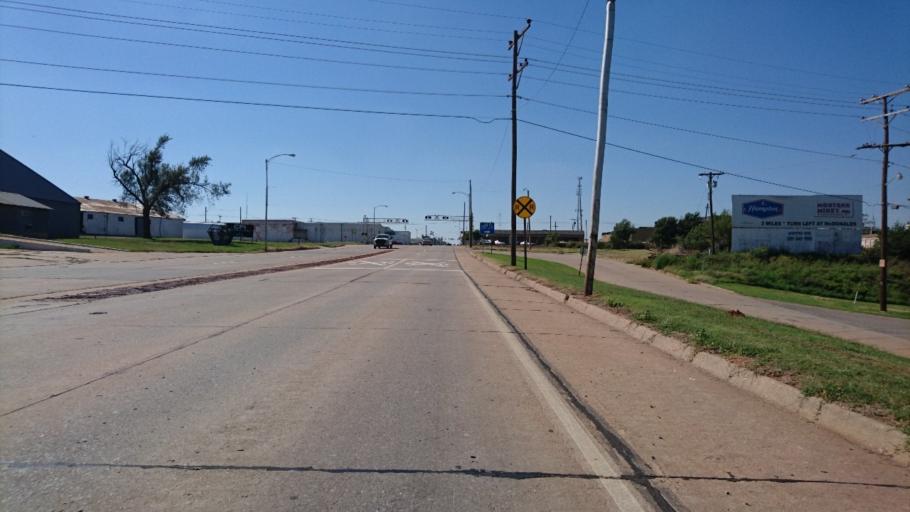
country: US
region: Oklahoma
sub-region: Custer County
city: Clinton
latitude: 35.5155
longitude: -98.9583
